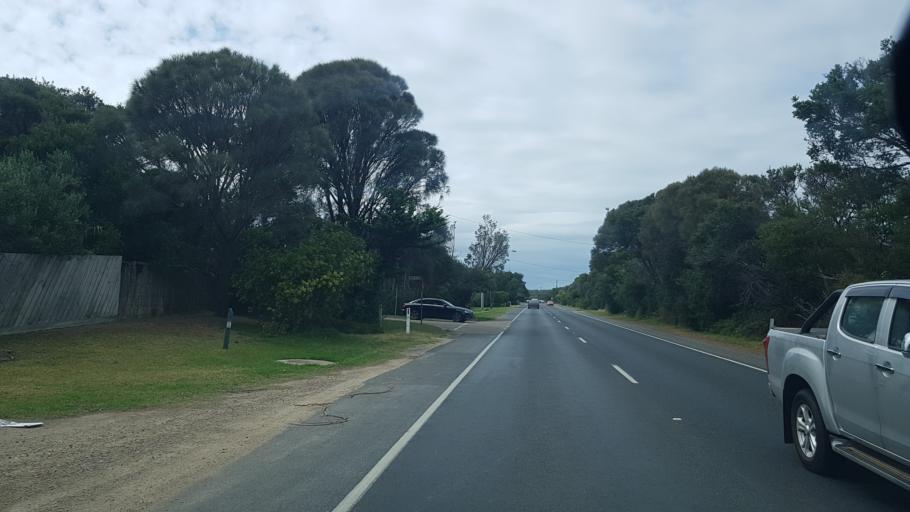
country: AU
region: Victoria
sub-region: Mornington Peninsula
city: Blairgowrie
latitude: -38.3742
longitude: 144.7779
